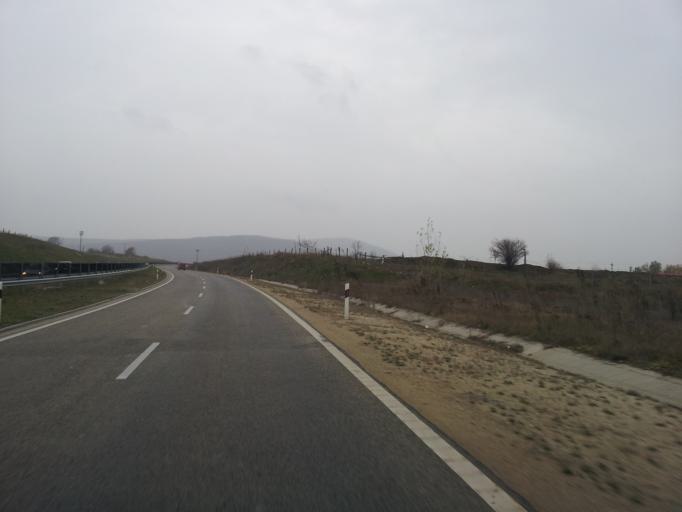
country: HU
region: Veszprem
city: Herend
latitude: 47.1194
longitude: 17.8264
